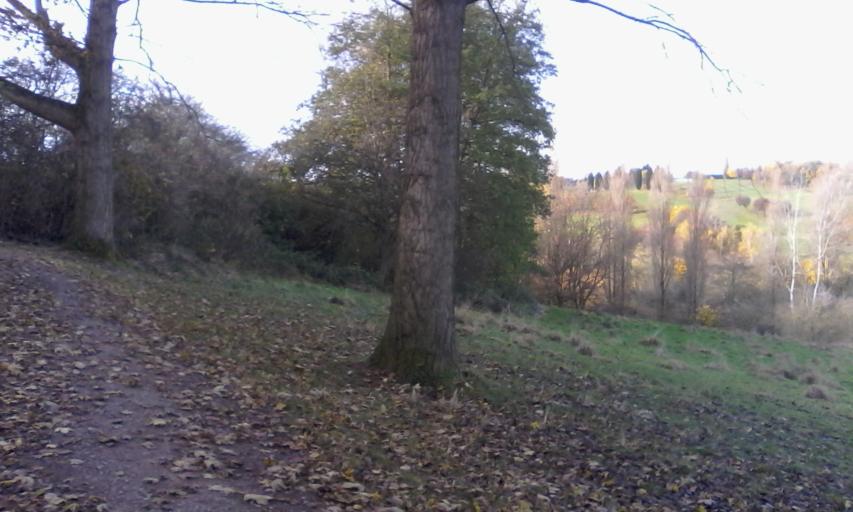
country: GB
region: England
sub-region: Nottinghamshire
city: Arnold
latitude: 52.9838
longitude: -1.1020
